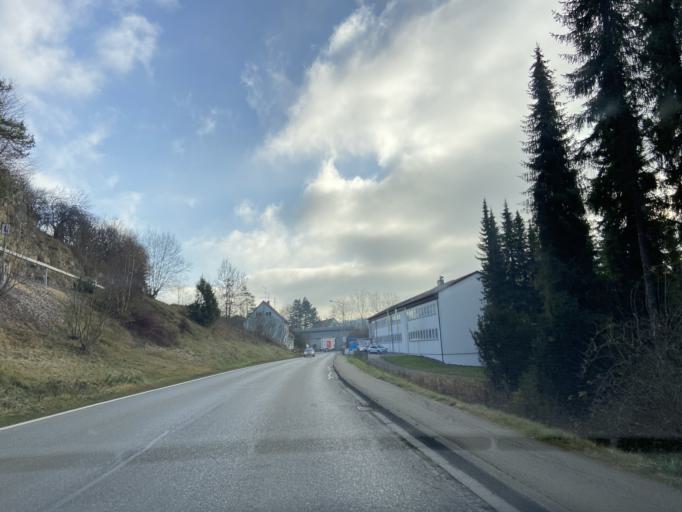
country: DE
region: Baden-Wuerttemberg
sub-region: Tuebingen Region
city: Gammertingen
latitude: 48.2530
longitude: 9.2128
